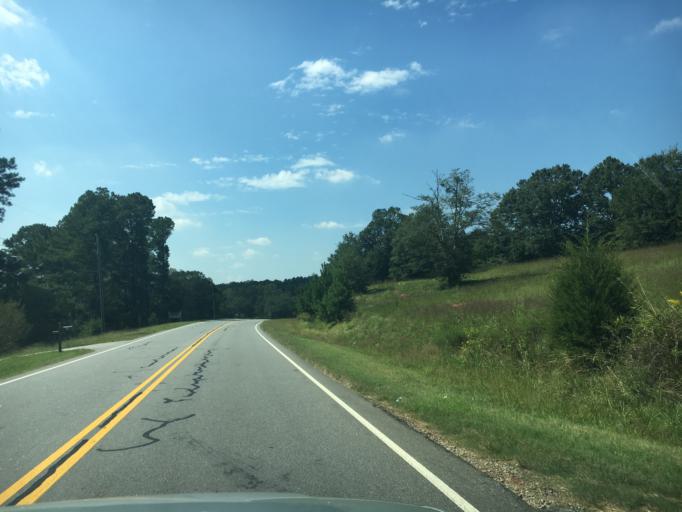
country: US
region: Georgia
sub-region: Hart County
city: Hartwell
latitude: 34.3621
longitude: -82.9707
